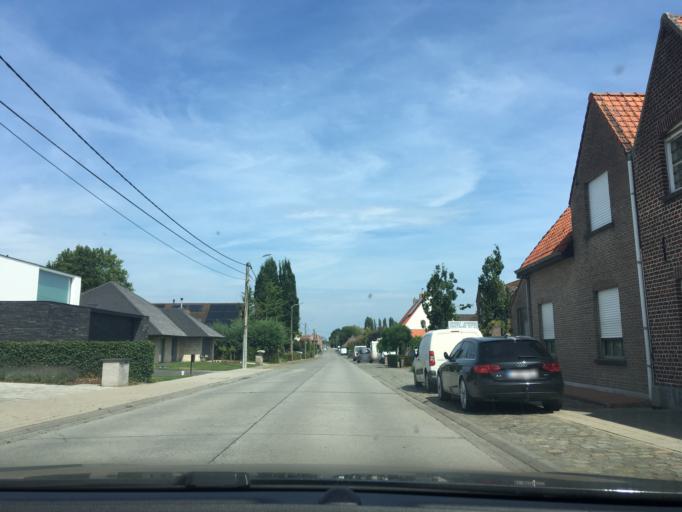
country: BE
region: Flanders
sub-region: Provincie West-Vlaanderen
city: Ledegem
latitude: 50.8965
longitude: 3.1224
